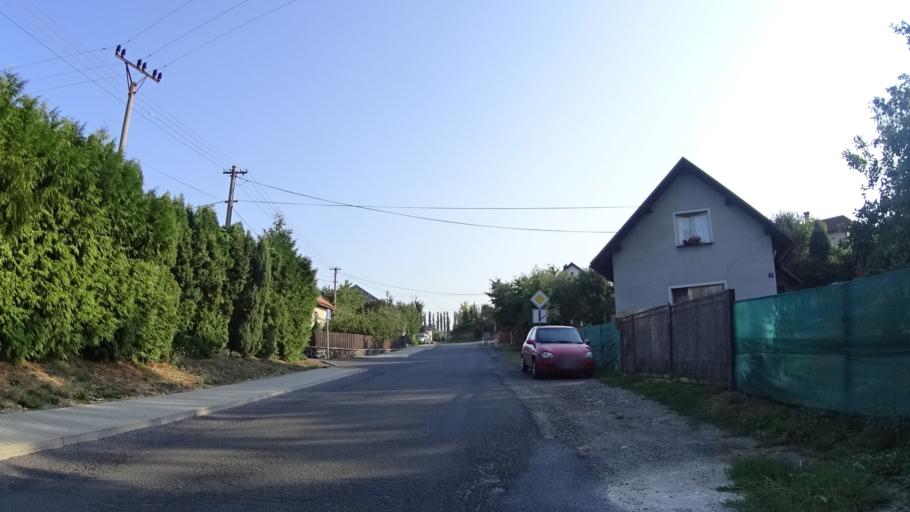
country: CZ
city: Ohrazenice
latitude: 50.5997
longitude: 15.1271
